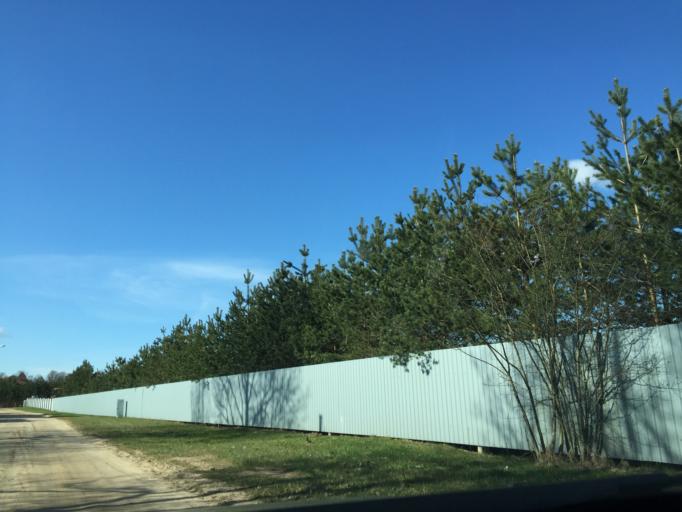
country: LV
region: Kekava
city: Kekava
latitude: 56.8486
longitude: 24.2032
